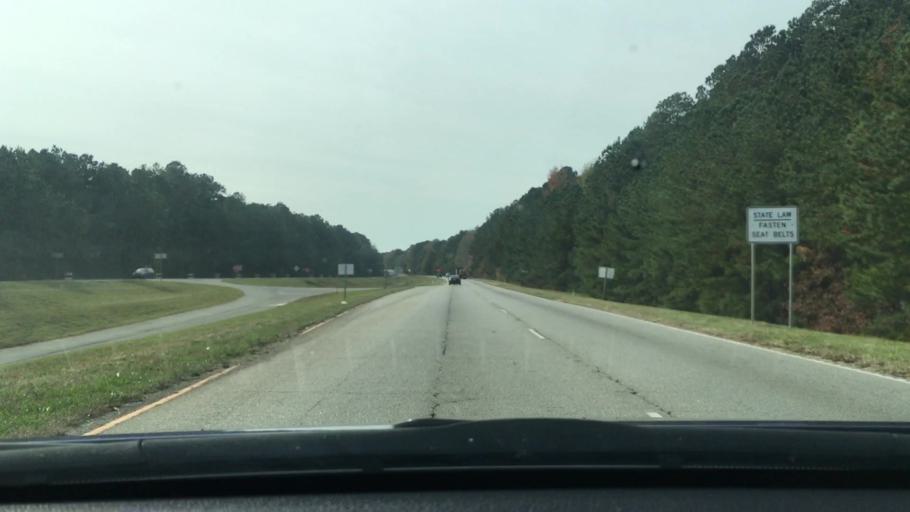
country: US
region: South Carolina
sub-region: Sumter County
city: Stateburg
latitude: 33.9471
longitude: -80.6321
